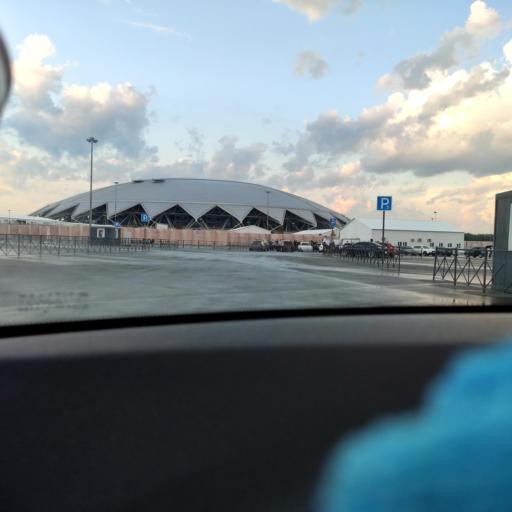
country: RU
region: Samara
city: Samara
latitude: 53.2738
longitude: 50.2333
